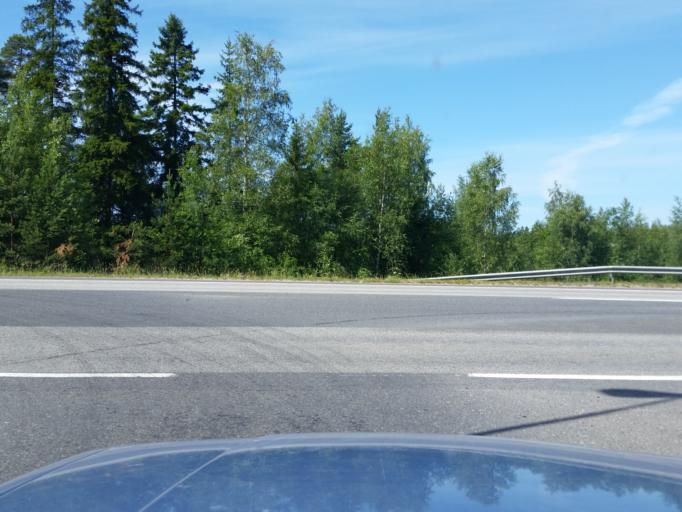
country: FI
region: Varsinais-Suomi
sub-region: Turku
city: Kaarina
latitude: 60.4253
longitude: 22.3804
